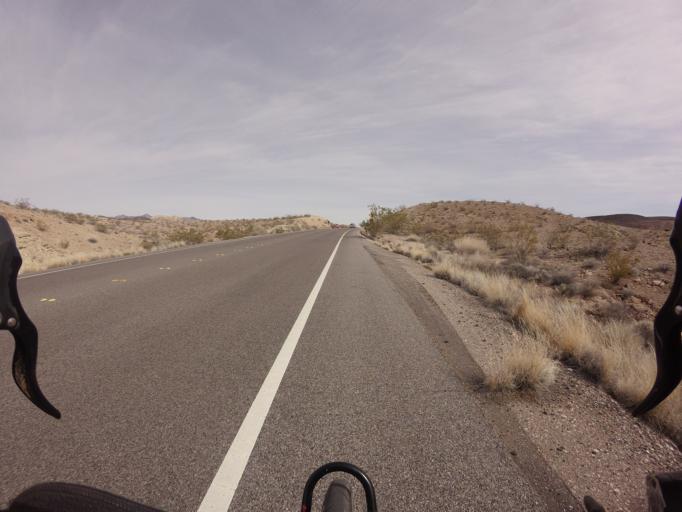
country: US
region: Nevada
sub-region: Clark County
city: Boulder City
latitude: 36.1769
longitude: -114.7687
